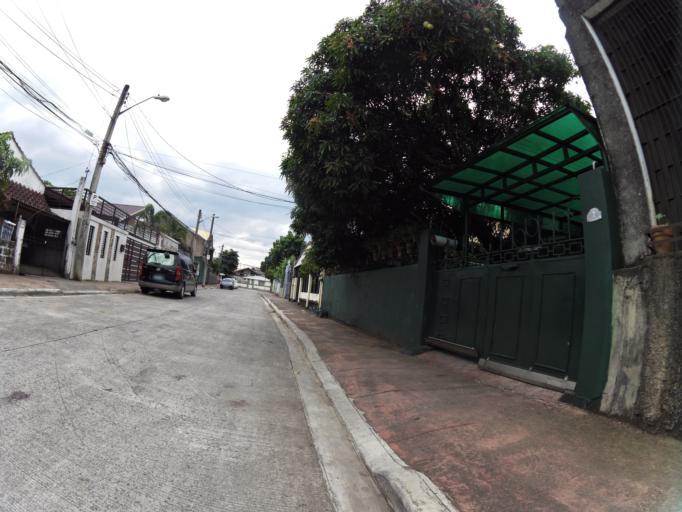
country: PH
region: Calabarzon
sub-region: Province of Rizal
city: Antipolo
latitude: 14.6396
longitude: 121.1160
